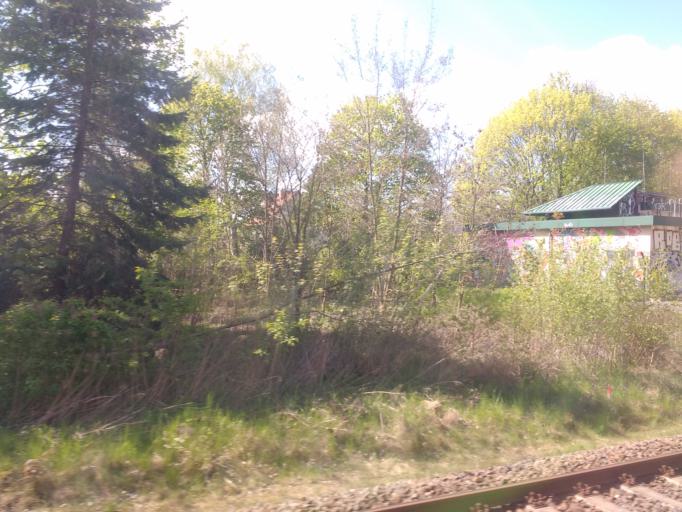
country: DE
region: Berlin
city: Grunau
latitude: 52.4151
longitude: 13.5667
